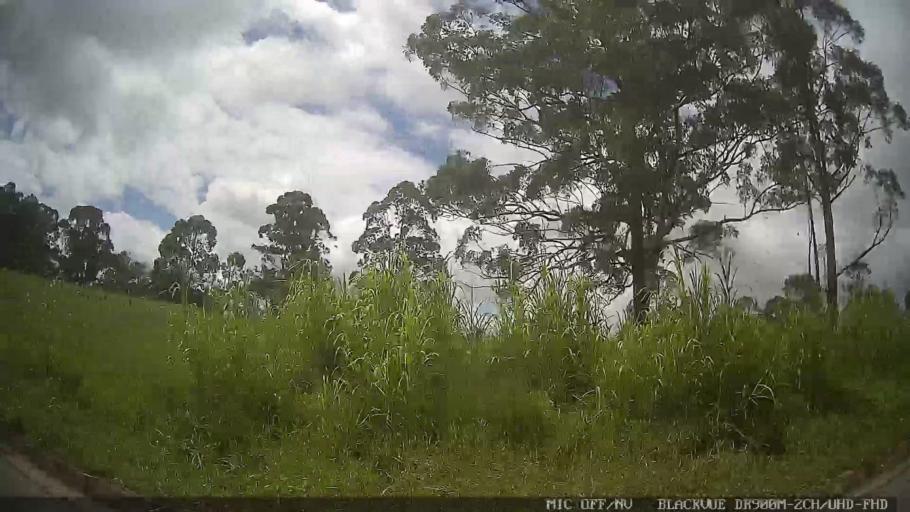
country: BR
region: Sao Paulo
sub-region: Braganca Paulista
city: Braganca Paulista
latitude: -22.8079
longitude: -46.5357
